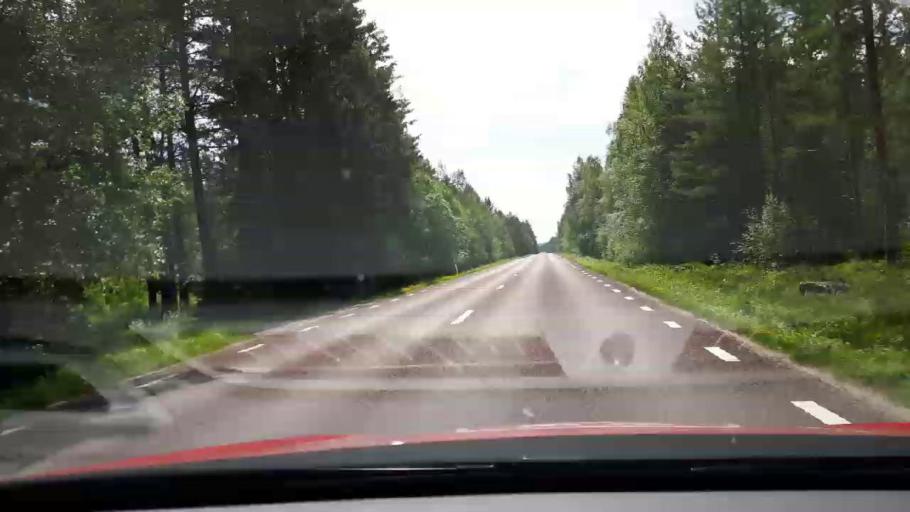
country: SE
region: Jaemtland
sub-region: Harjedalens Kommun
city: Sveg
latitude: 62.1163
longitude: 14.9701
